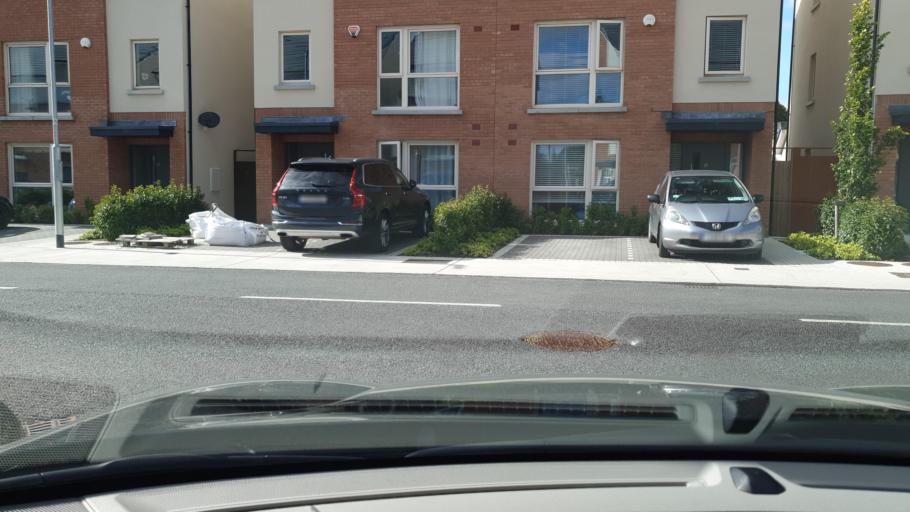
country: IE
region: Leinster
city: Hartstown
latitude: 53.3860
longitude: -6.4302
